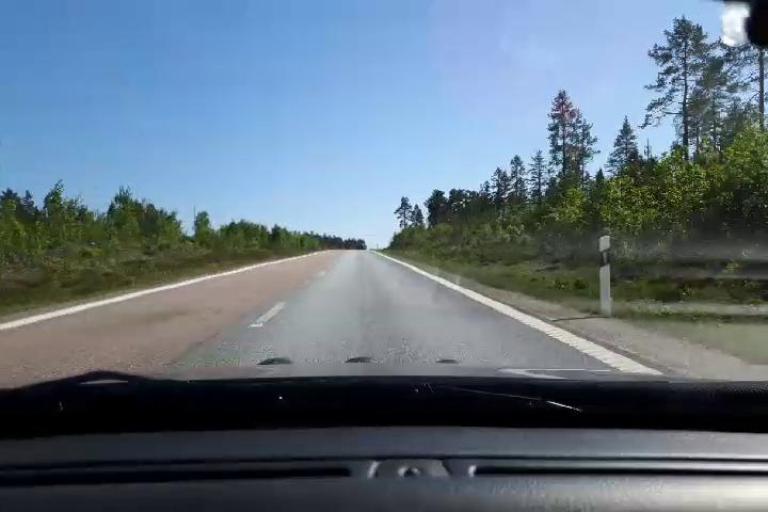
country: SE
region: Gaevleborg
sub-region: Soderhamns Kommun
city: Soderhamn
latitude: 61.3940
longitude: 16.9921
